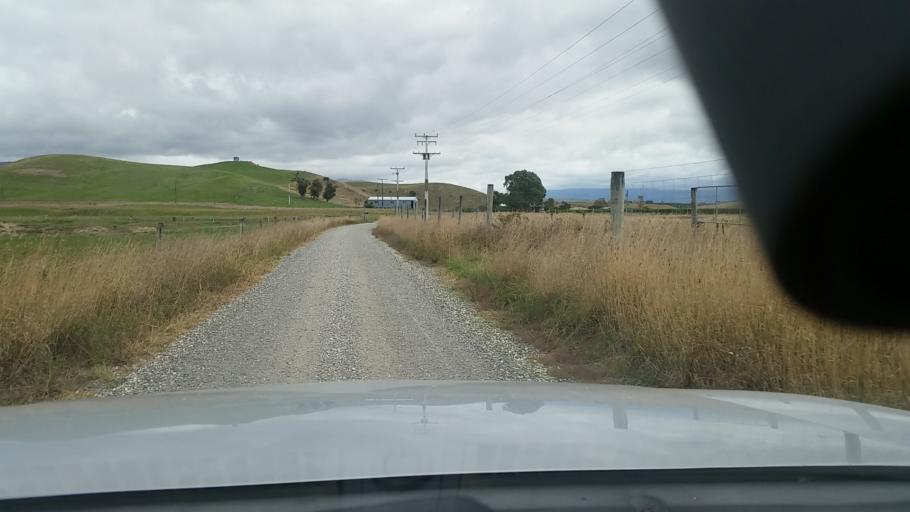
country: NZ
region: Marlborough
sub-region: Marlborough District
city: Blenheim
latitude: -41.7007
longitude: 174.1159
